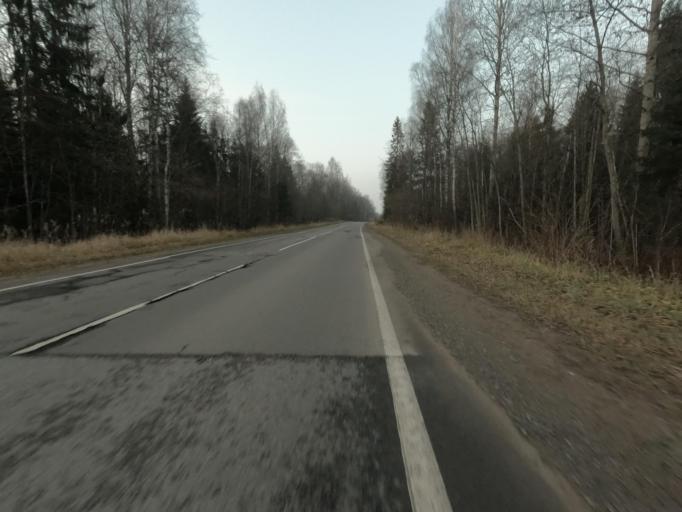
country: RU
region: Leningrad
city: Kirovsk
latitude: 59.8518
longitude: 30.9902
